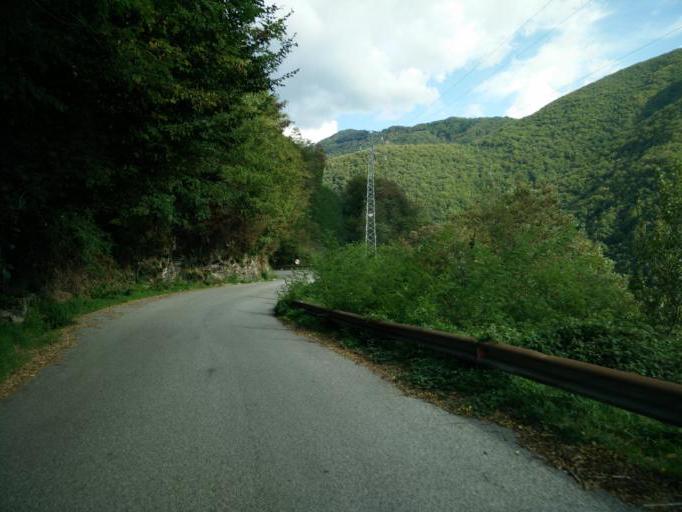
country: IT
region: Tuscany
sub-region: Provincia di Massa-Carrara
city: Zeri
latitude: 44.3518
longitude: 9.7950
